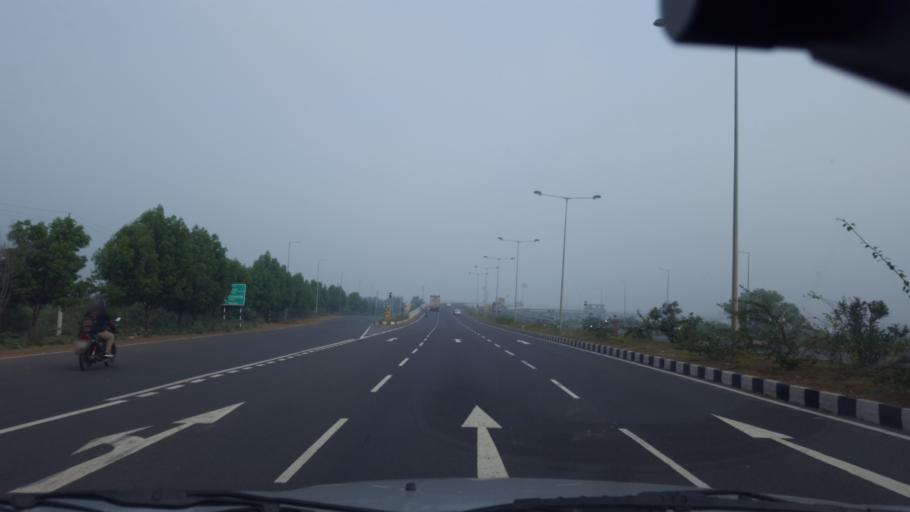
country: IN
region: Andhra Pradesh
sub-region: Prakasam
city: Ongole
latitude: 15.4662
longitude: 80.0483
